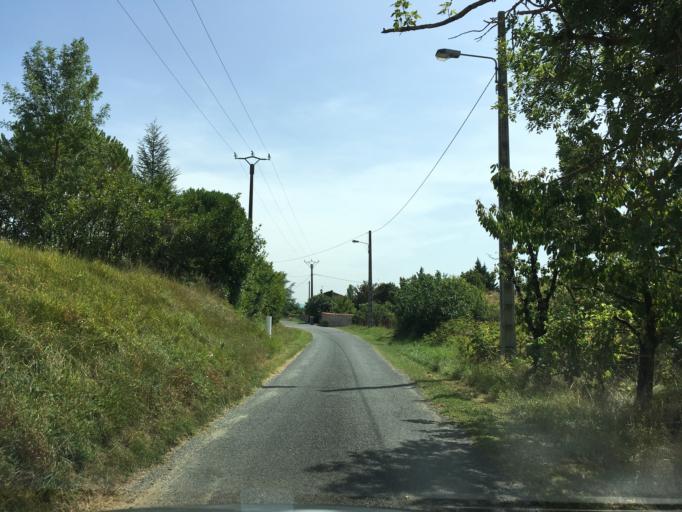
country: FR
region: Midi-Pyrenees
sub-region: Departement du Tarn
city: Castres
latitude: 43.6324
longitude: 2.2276
